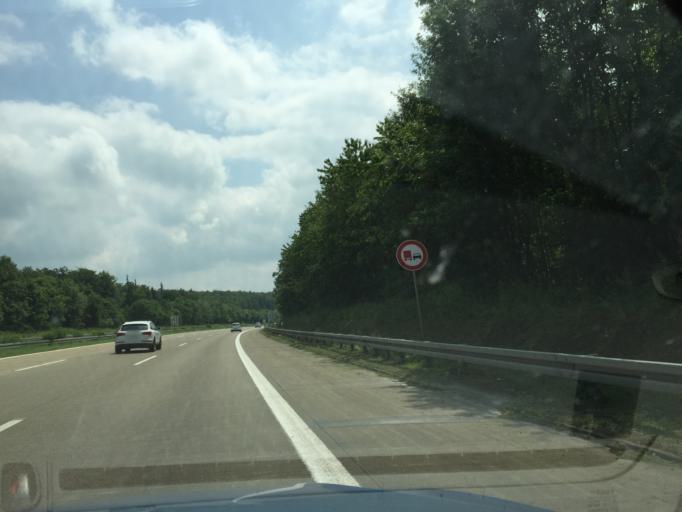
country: DE
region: Baden-Wuerttemberg
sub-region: Regierungsbezirk Stuttgart
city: Westhausen
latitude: 48.8573
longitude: 10.1972
